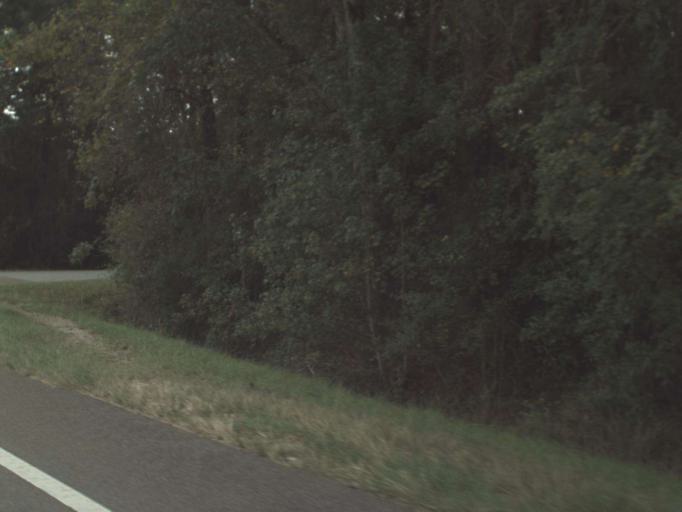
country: US
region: Florida
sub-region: Walton County
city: DeFuniak Springs
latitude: 30.6951
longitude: -85.9364
